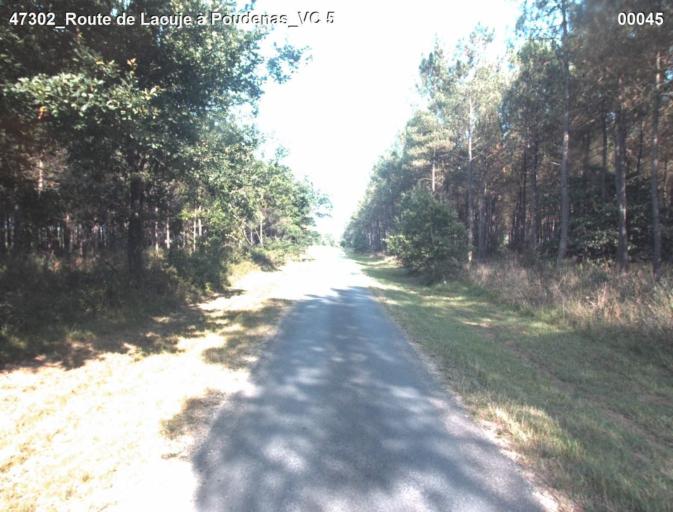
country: FR
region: Aquitaine
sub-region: Departement du Lot-et-Garonne
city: Mezin
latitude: 44.0638
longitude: 0.1599
